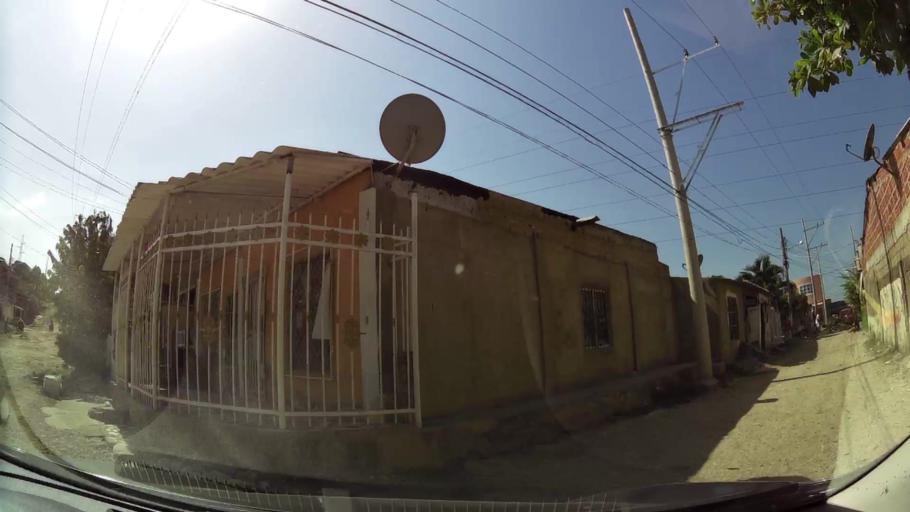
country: CO
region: Bolivar
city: Cartagena
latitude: 10.3707
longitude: -75.4702
